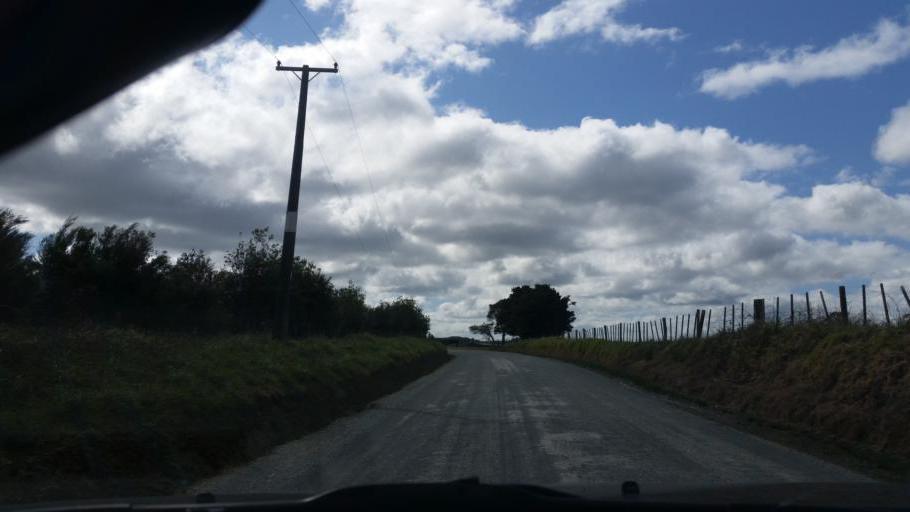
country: NZ
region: Auckland
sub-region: Auckland
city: Wellsford
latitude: -36.1460
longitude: 174.5067
